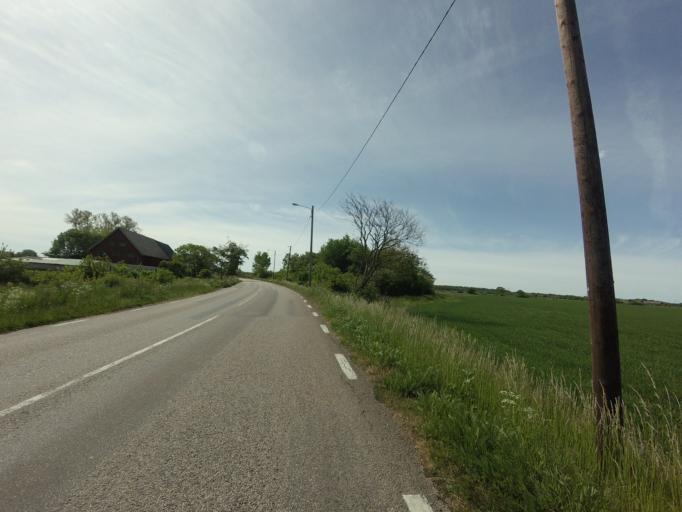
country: SE
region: Skane
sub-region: Helsingborg
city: Odakra
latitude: 56.1492
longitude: 12.6781
